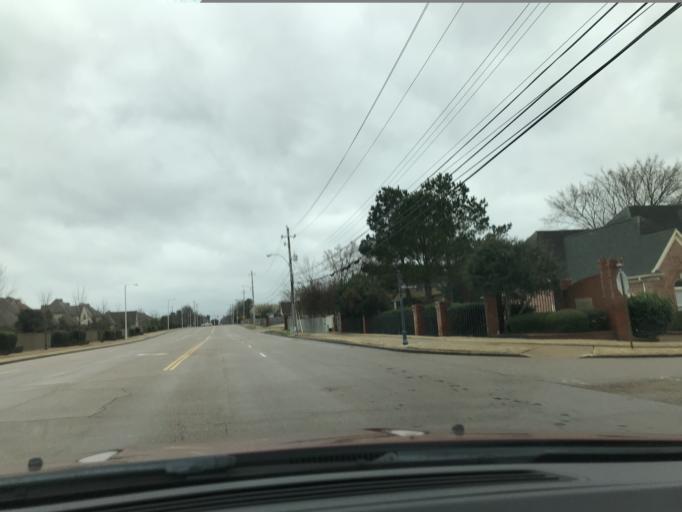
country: US
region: Tennessee
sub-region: Shelby County
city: Collierville
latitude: 35.0781
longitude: -89.6853
